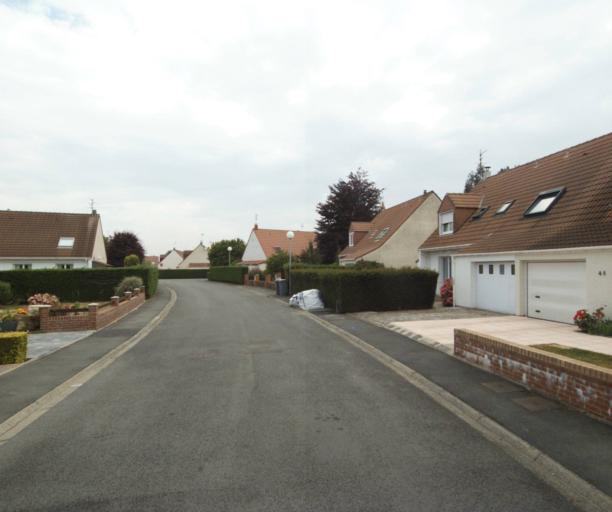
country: FR
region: Nord-Pas-de-Calais
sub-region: Departement du Nord
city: Santes
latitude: 50.5897
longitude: 2.9597
